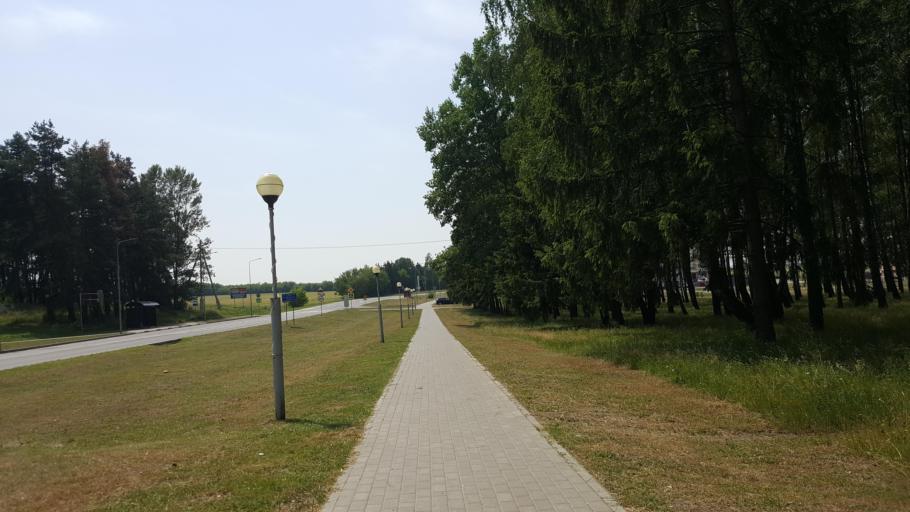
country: BY
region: Brest
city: Kamyanyets
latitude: 52.3905
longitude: 23.8204
